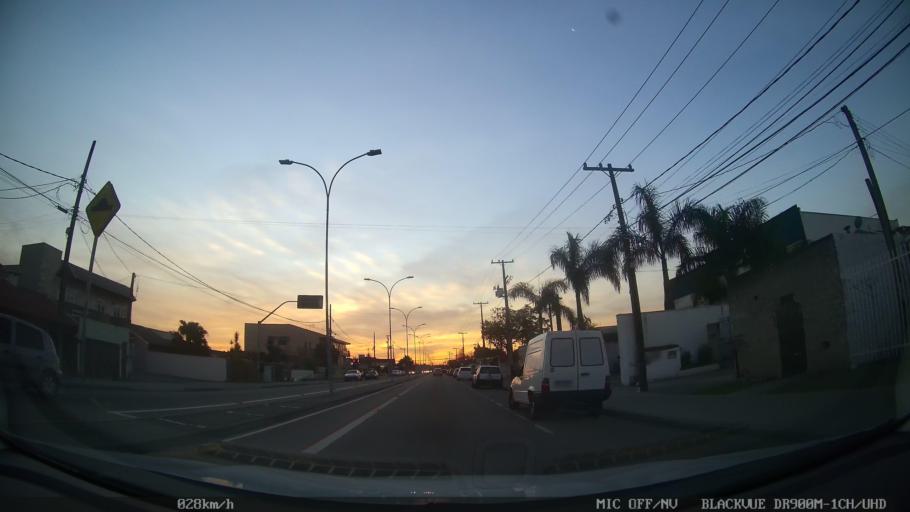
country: BR
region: Parana
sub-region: Pinhais
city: Pinhais
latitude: -25.4397
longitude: -49.1965
